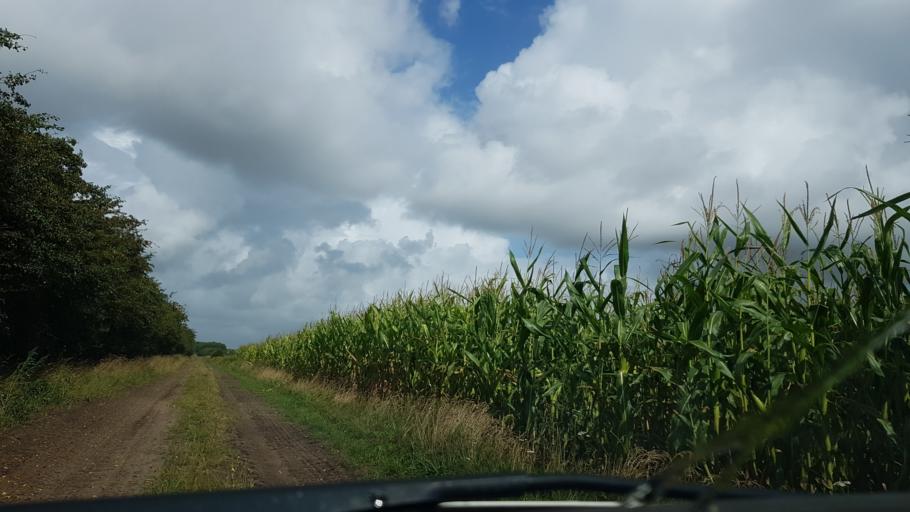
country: DK
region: South Denmark
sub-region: Esbjerg Kommune
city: Ribe
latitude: 55.2509
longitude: 8.7676
